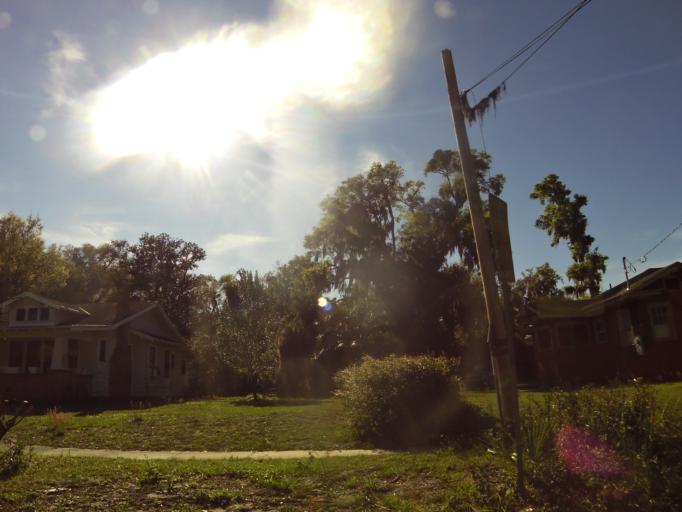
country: US
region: Florida
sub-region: Duval County
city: Jacksonville
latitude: 30.3831
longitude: -81.6472
